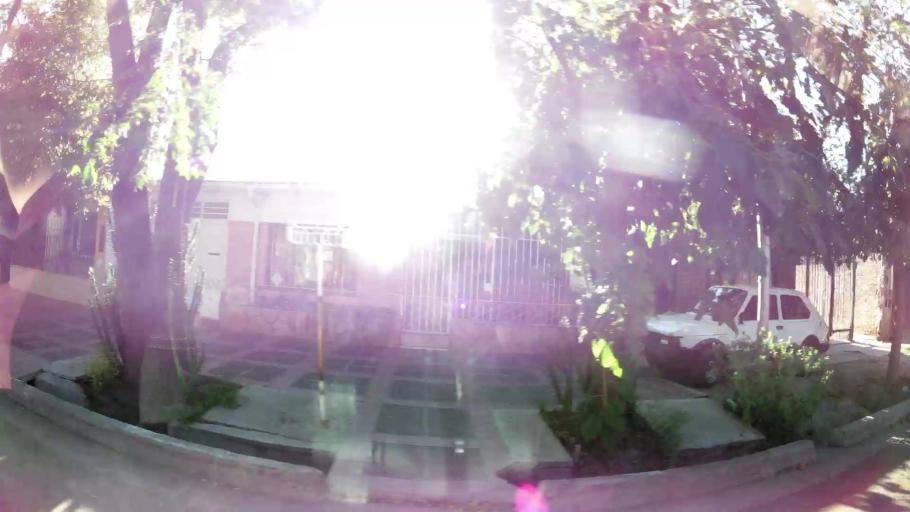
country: AR
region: Mendoza
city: Las Heras
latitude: -32.8566
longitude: -68.8194
